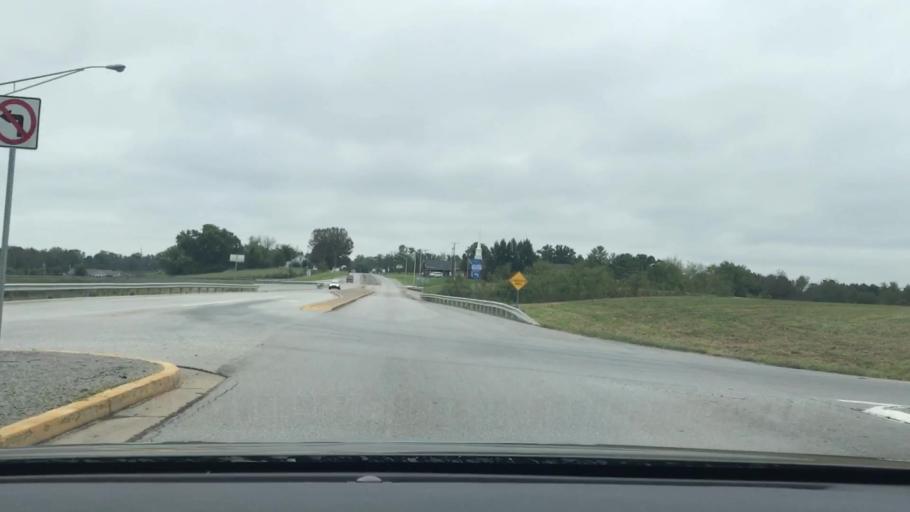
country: US
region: Kentucky
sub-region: Adair County
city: Columbia
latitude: 37.0894
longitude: -85.3038
